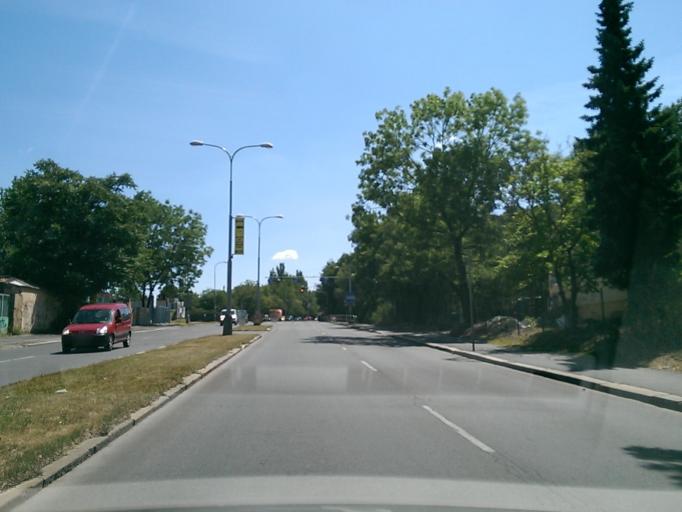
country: CZ
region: Praha
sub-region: Praha 8
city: Liben
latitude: 50.0999
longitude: 14.4920
